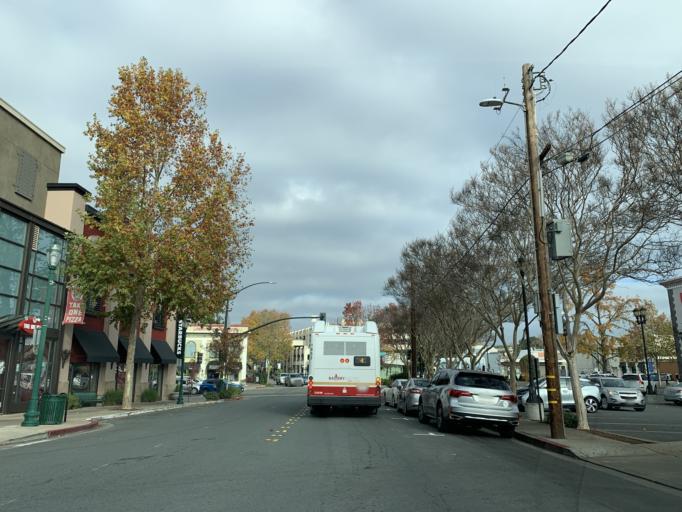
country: US
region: California
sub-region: Contra Costa County
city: Walnut Creek
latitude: 37.8967
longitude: -122.0614
